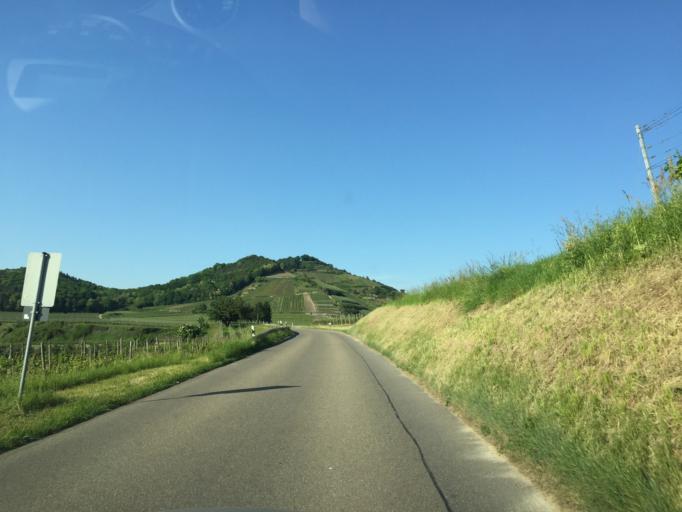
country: DE
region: Baden-Wuerttemberg
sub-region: Freiburg Region
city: Breisach am Rhein
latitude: 48.0624
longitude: 7.6112
